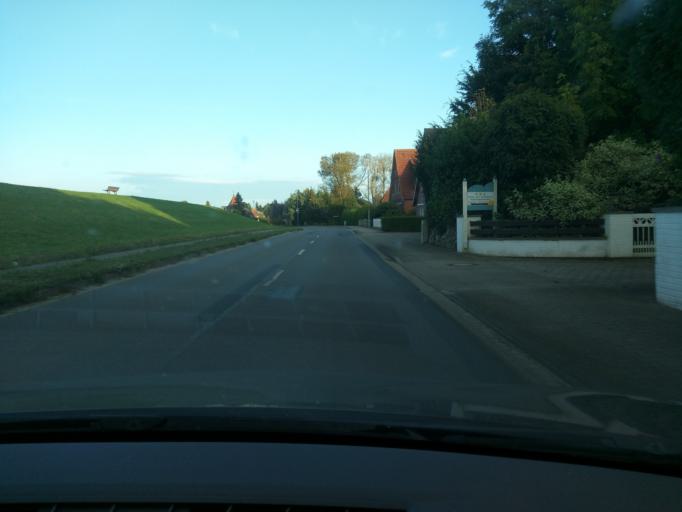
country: DE
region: Lower Saxony
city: Artlenburg
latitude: 53.3761
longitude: 10.4797
